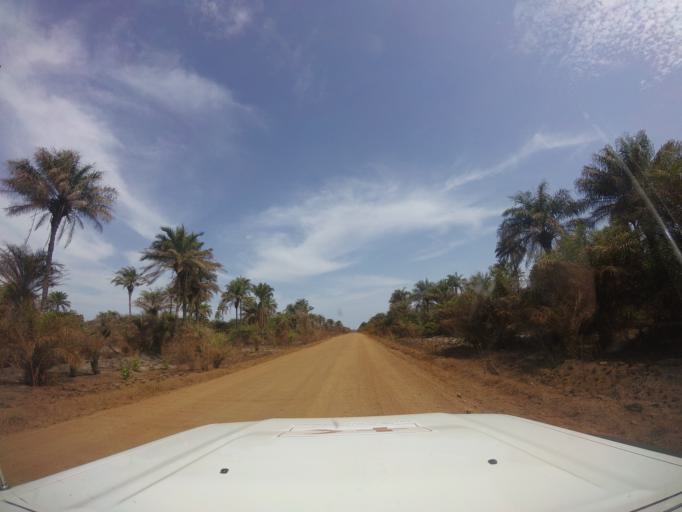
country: LR
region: Grand Cape Mount
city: Robertsport
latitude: 6.7007
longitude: -11.2888
